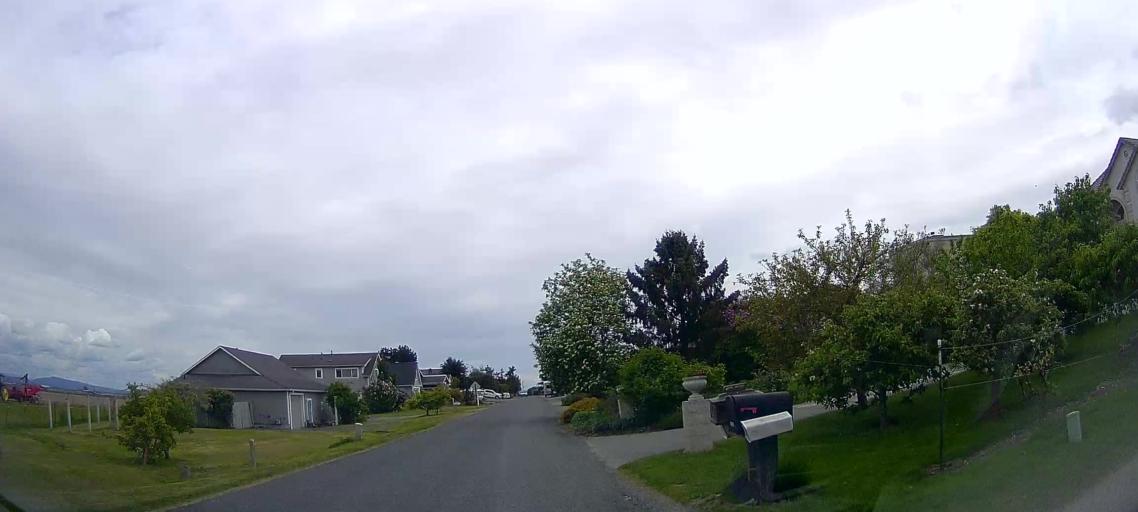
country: US
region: Washington
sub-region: Skagit County
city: Anacortes
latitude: 48.4332
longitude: -122.4976
